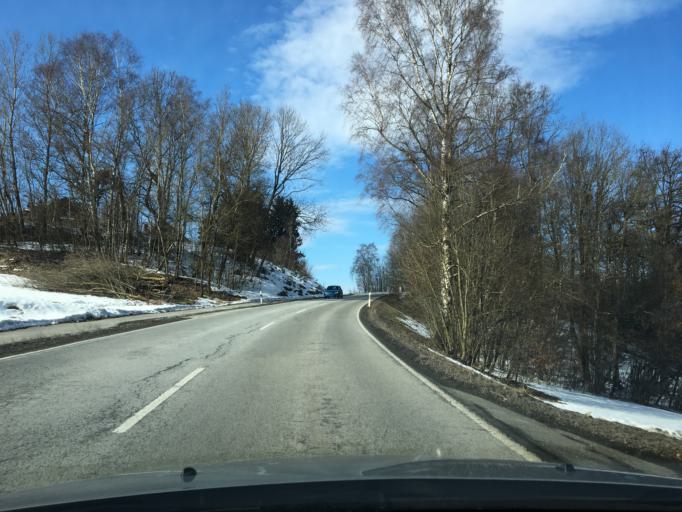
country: DE
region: Bavaria
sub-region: Lower Bavaria
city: Freyung
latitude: 48.8063
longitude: 13.5366
